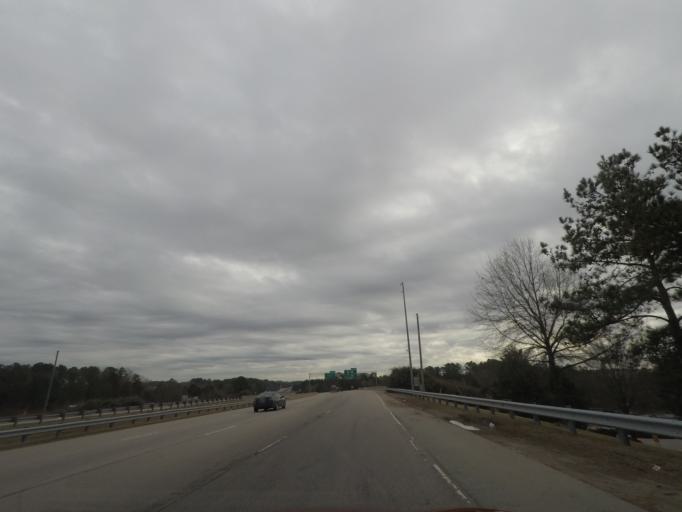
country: US
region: North Carolina
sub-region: Durham County
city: Durham
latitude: 36.0170
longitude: -78.9523
